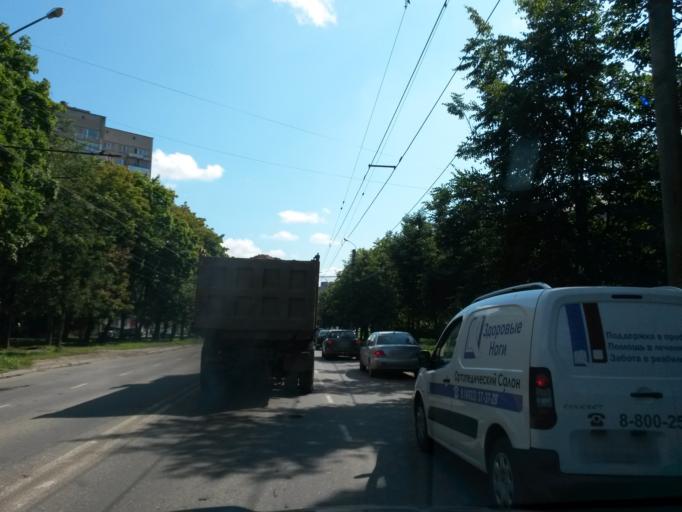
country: RU
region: Ivanovo
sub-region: Gorod Ivanovo
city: Ivanovo
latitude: 57.0107
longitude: 40.9847
